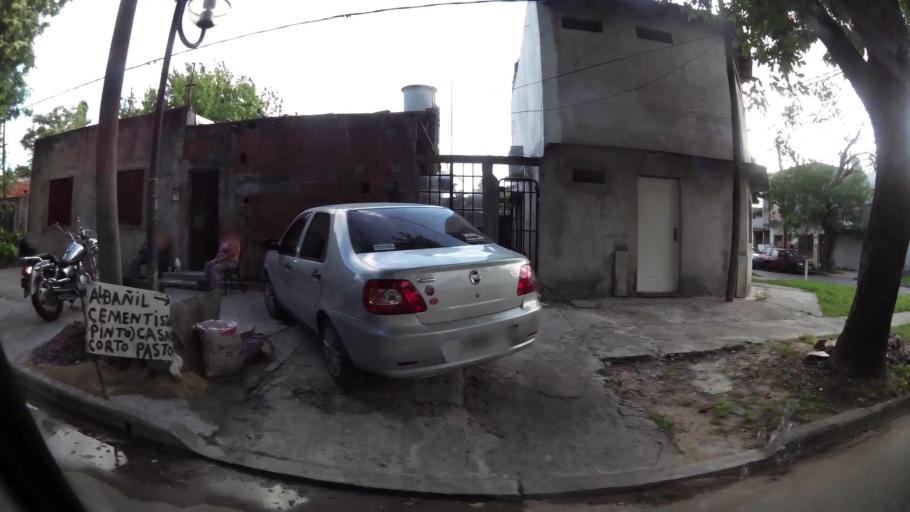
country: AR
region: Buenos Aires
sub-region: Partido de La Plata
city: La Plata
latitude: -34.8940
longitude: -57.9573
